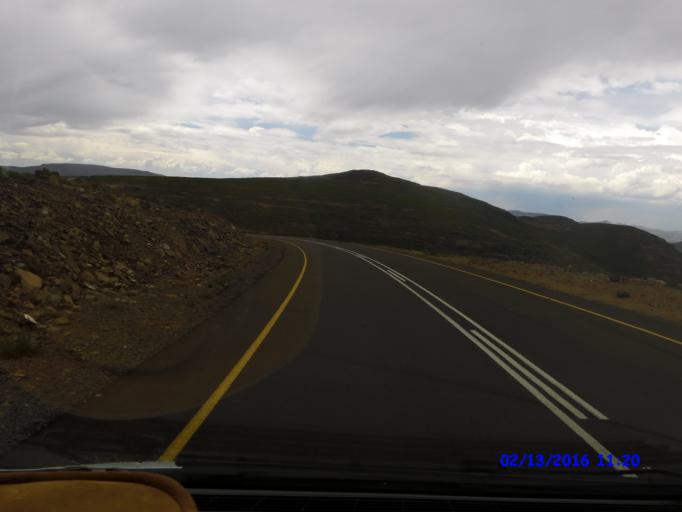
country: LS
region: Maseru
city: Nako
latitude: -29.7551
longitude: 27.9725
